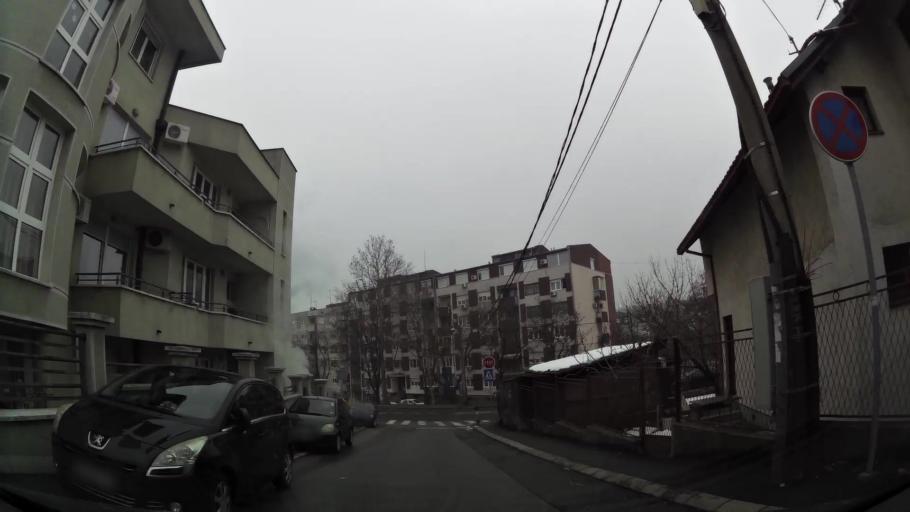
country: RS
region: Central Serbia
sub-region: Belgrade
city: Vozdovac
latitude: 44.7761
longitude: 20.4807
